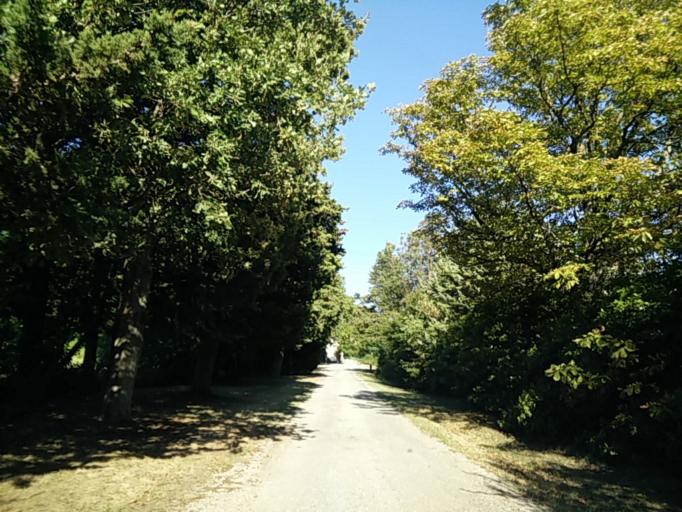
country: FR
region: Rhone-Alpes
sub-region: Departement de la Drome
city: La Begude-de-Mazenc
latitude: 44.5465
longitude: 4.9305
